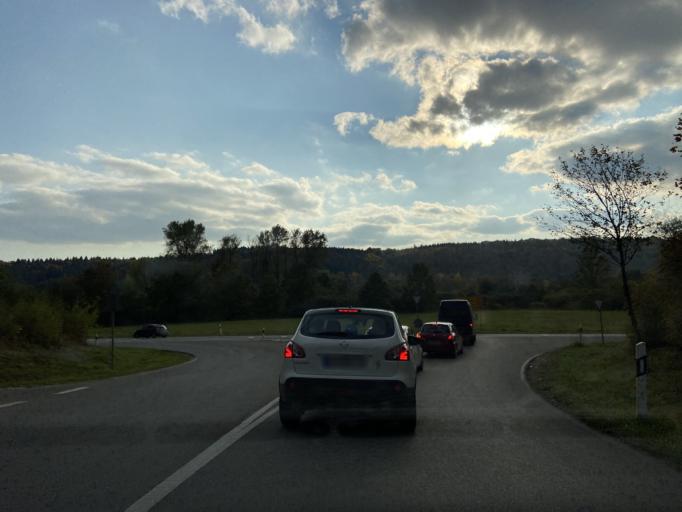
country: DE
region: Baden-Wuerttemberg
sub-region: Tuebingen Region
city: Sigmaringen
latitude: 48.0792
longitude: 9.2390
